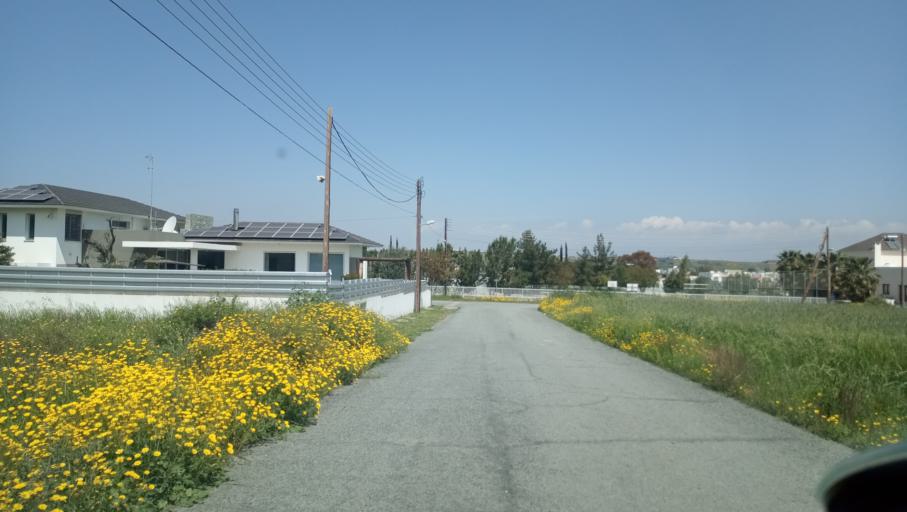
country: CY
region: Lefkosia
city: Dali
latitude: 35.0135
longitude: 33.3999
